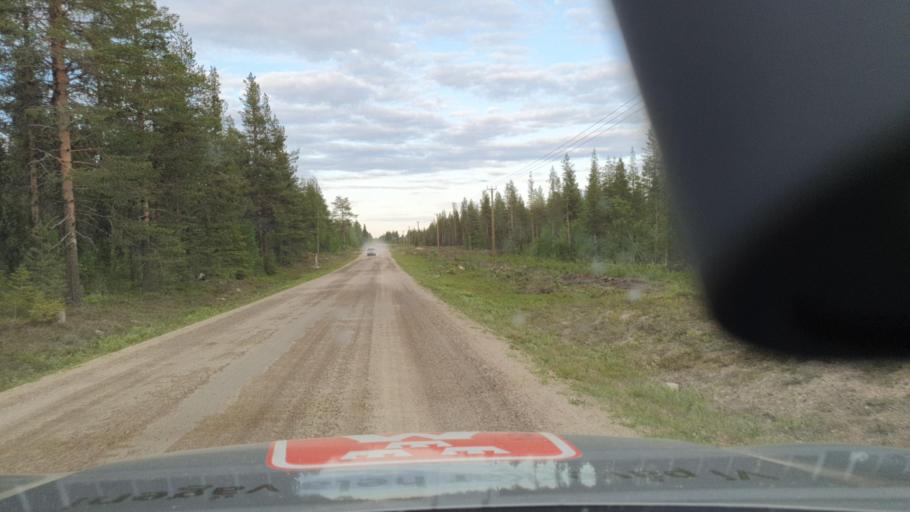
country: SE
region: Norrbotten
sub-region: Gallivare Kommun
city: Gaellivare
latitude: 66.7422
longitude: 21.1199
